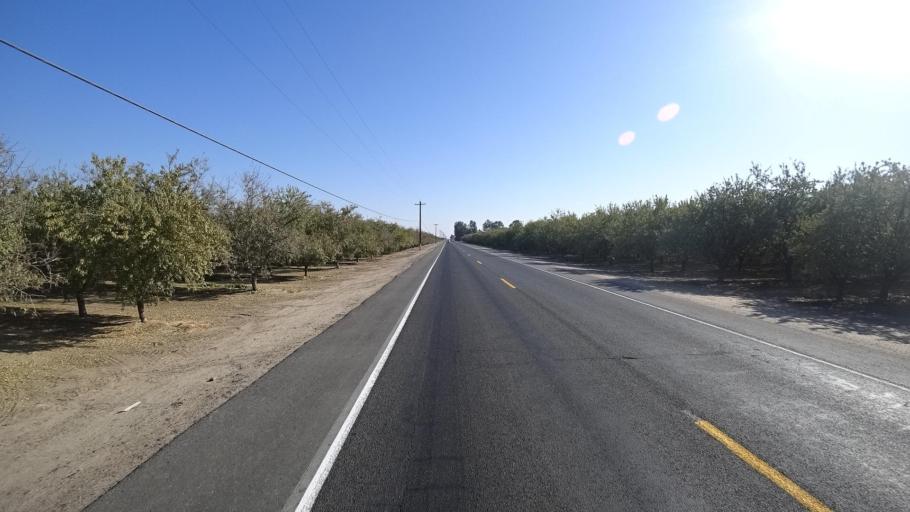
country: US
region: California
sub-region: Kern County
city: Delano
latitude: 35.7178
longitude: -119.3249
